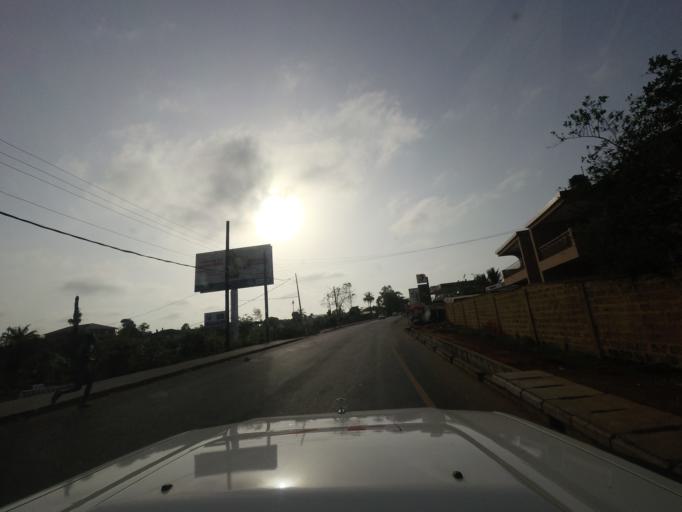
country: SL
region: Western Area
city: Freetown
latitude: 8.4918
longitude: -13.2848
